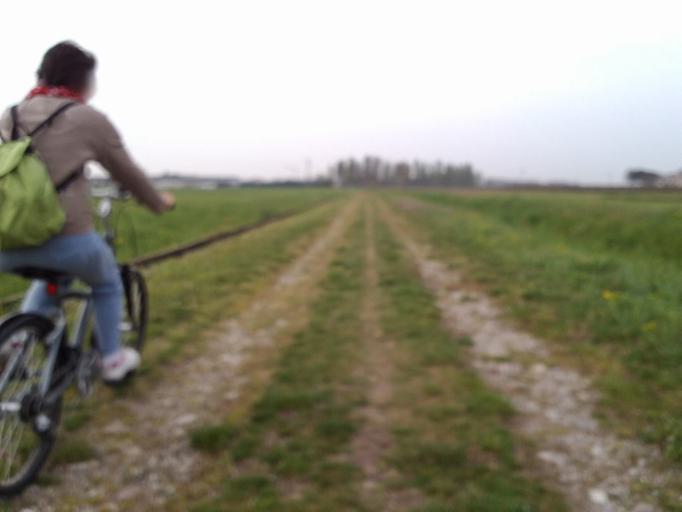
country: IT
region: Veneto
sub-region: Provincia di Verona
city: Villafranca di Verona
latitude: 45.3332
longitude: 10.8553
